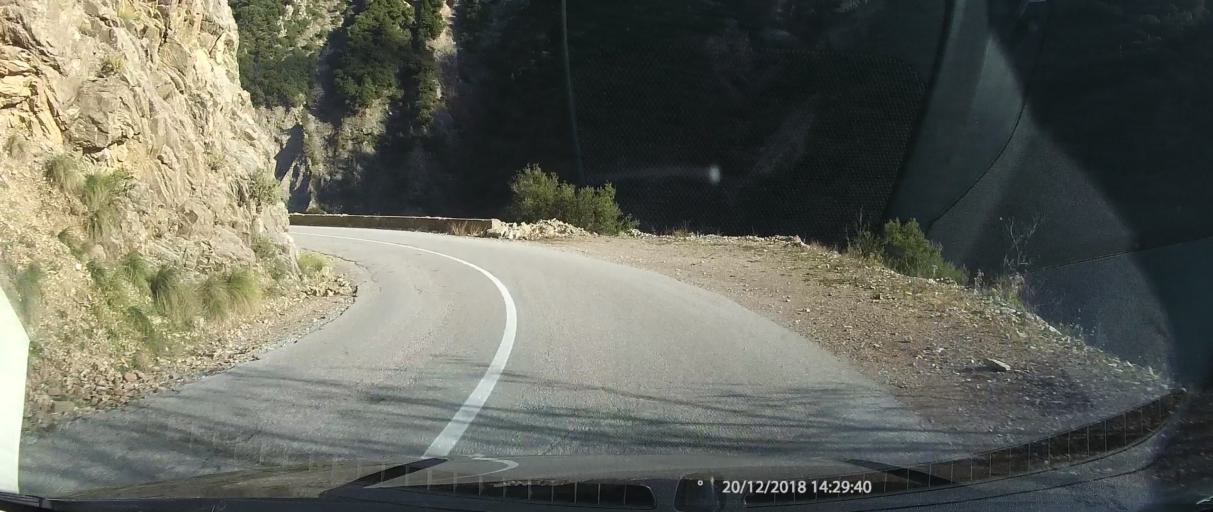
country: GR
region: Central Greece
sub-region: Nomos Evrytanias
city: Karpenisi
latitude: 38.7904
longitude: 21.6966
